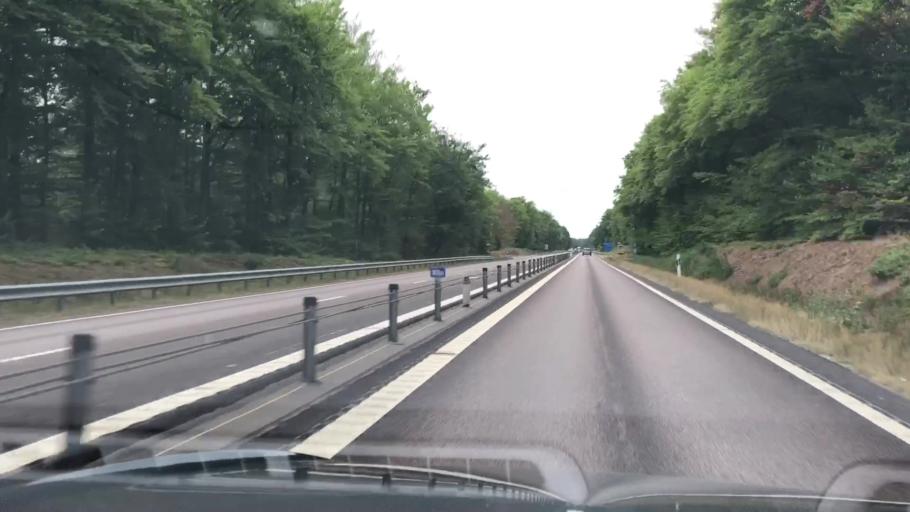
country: SE
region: Blekinge
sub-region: Karlskrona Kommun
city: Jaemjoe
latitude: 56.2373
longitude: 15.9240
